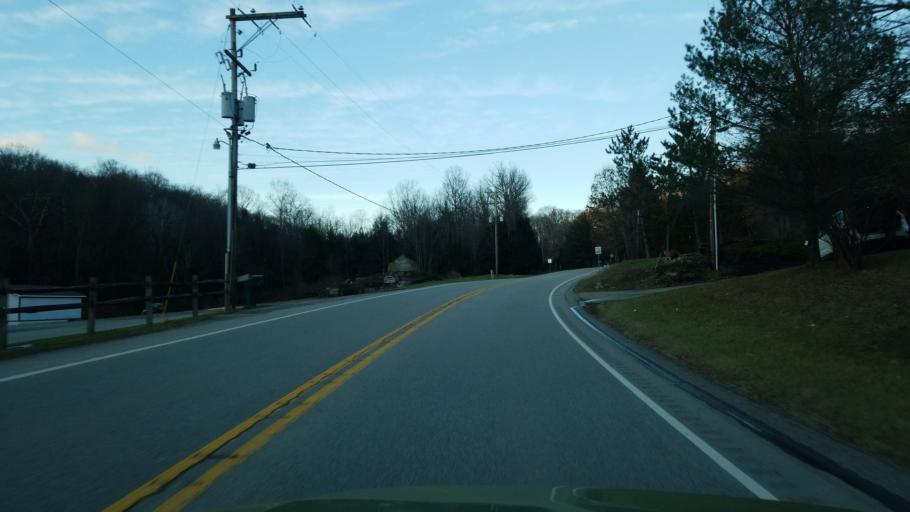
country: US
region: Pennsylvania
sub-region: Indiana County
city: Chevy Chase Heights
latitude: 40.7282
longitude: -79.1020
